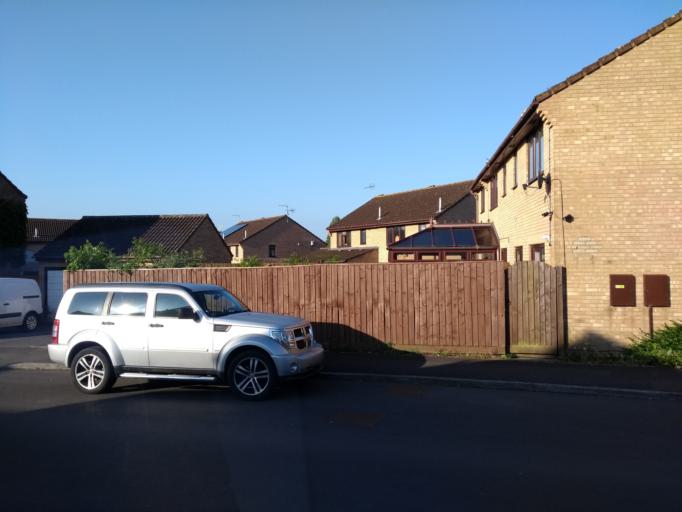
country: GB
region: England
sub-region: Somerset
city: Taunton
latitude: 51.0351
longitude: -3.0923
